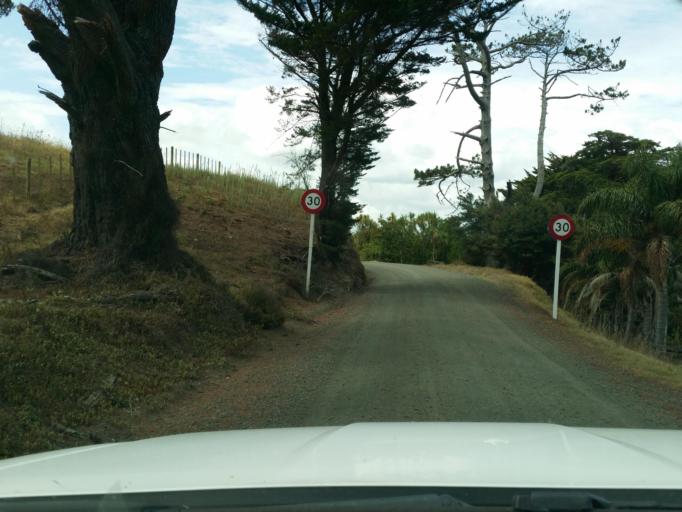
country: NZ
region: Auckland
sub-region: Auckland
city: Wellsford
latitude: -36.3629
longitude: 174.1780
